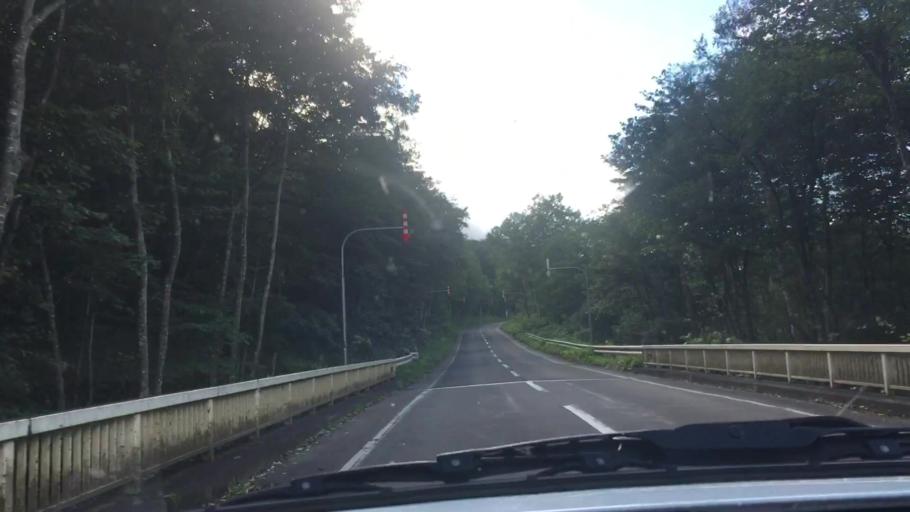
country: JP
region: Hokkaido
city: Otofuke
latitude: 43.1704
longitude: 142.9821
